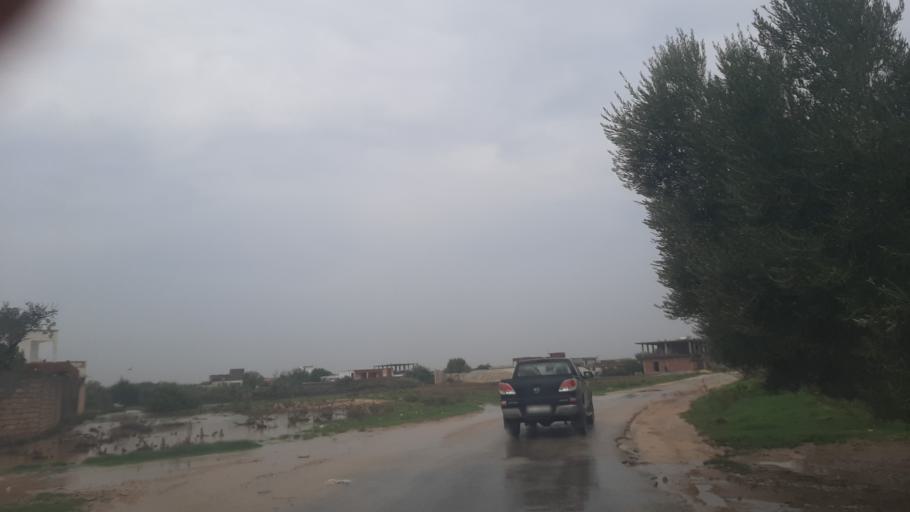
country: TN
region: Al Munastir
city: Sidi Bin Nur
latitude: 35.4745
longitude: 10.8777
